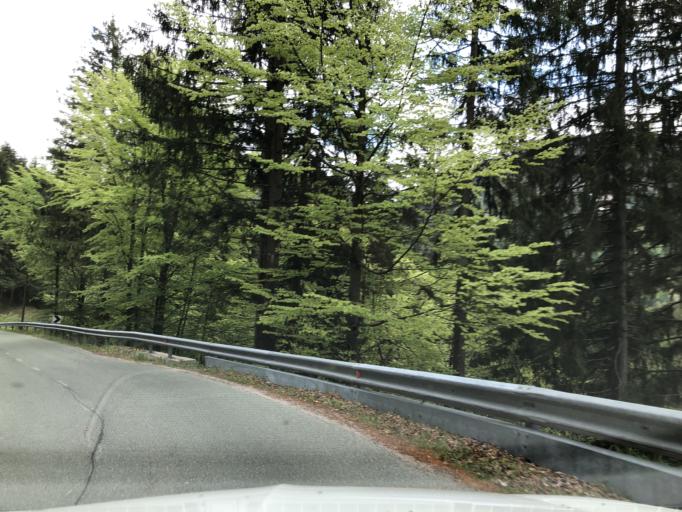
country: SI
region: Kranjska Gora
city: Kranjska Gora
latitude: 46.4999
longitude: 13.7560
